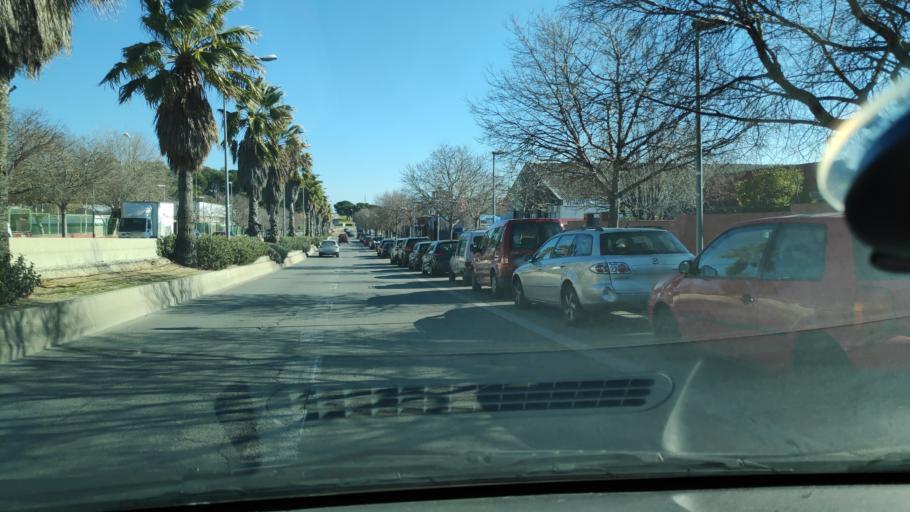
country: ES
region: Catalonia
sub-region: Provincia de Barcelona
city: Terrassa
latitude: 41.5576
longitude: 2.0363
